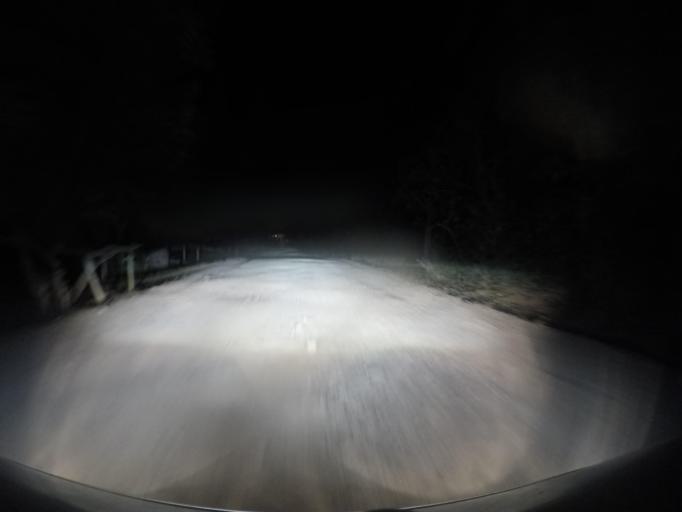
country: TL
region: Viqueque
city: Viqueque
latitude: -8.7948
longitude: 126.5573
